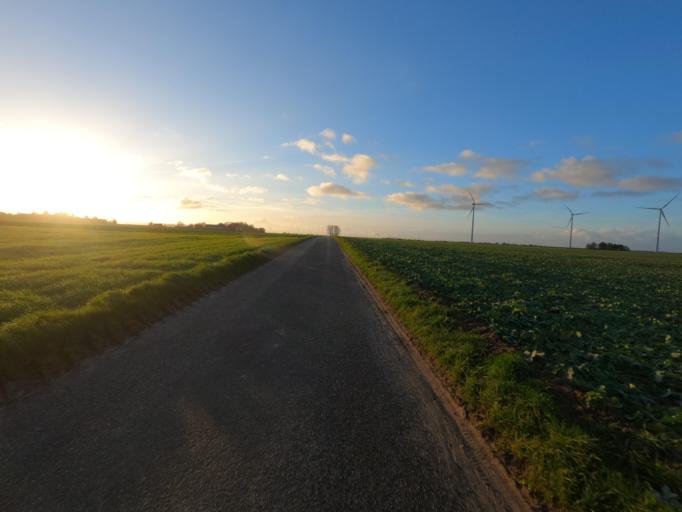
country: DE
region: North Rhine-Westphalia
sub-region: Regierungsbezirk Koln
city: Titz
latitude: 51.0234
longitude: 6.3607
